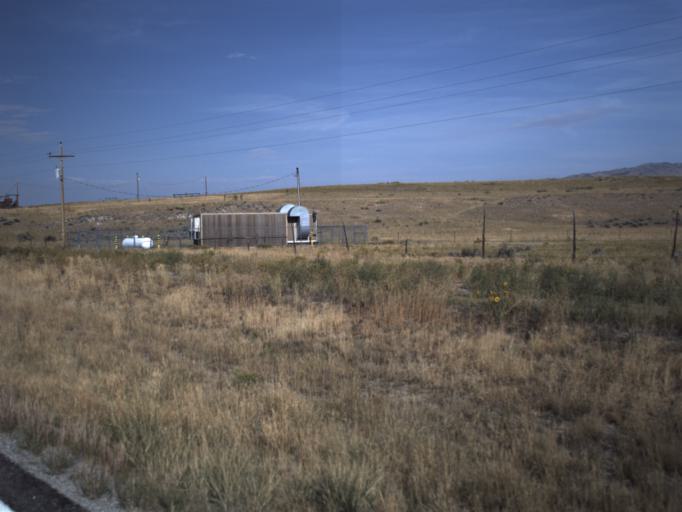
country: US
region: Idaho
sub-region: Oneida County
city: Malad City
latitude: 41.9653
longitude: -113.0512
